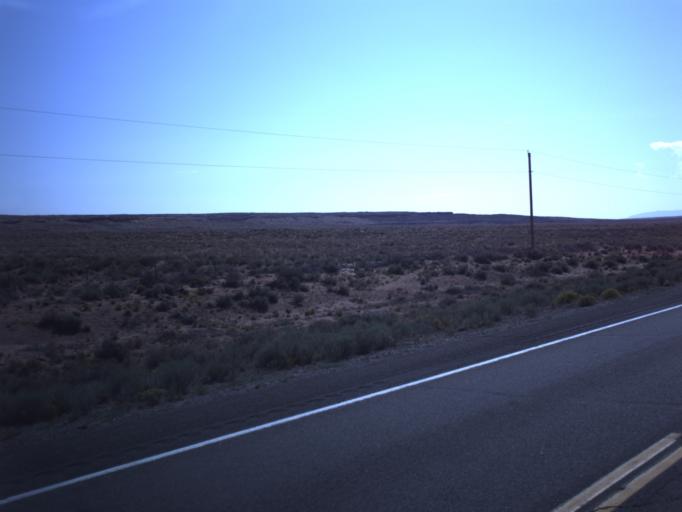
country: US
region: Utah
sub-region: San Juan County
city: Blanding
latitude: 37.1484
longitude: -109.5645
